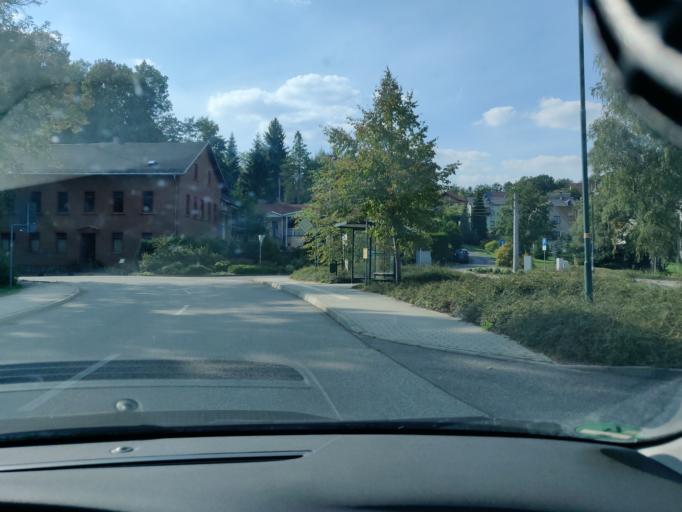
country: DE
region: Saxony
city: Mittweida
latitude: 51.0054
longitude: 12.9949
